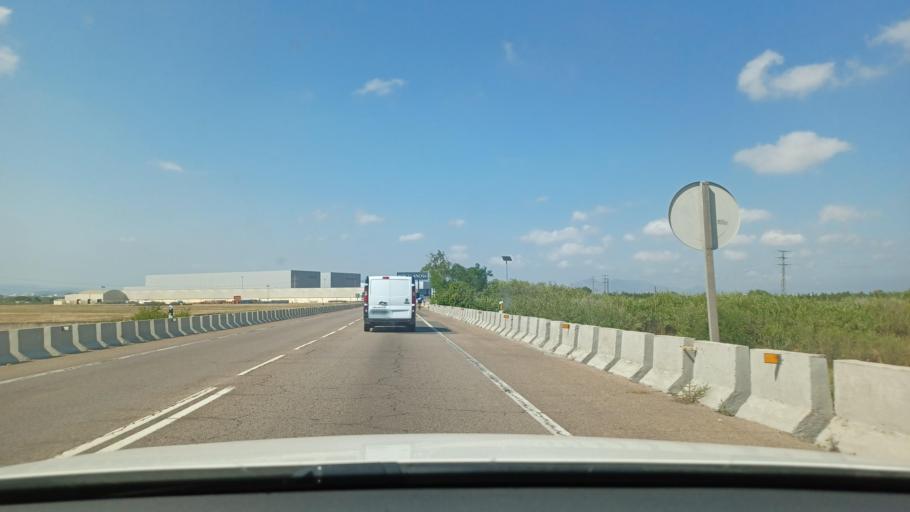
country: ES
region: Valencia
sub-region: Provincia de Castello
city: Alquerias del Nino Perdido
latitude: 39.9063
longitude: -0.1183
